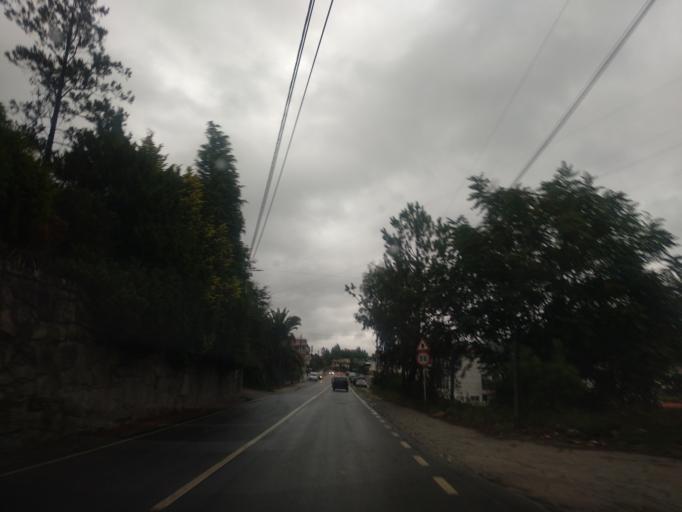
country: PT
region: Braga
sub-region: Guimaraes
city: Ponte
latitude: 41.4827
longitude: -8.3229
